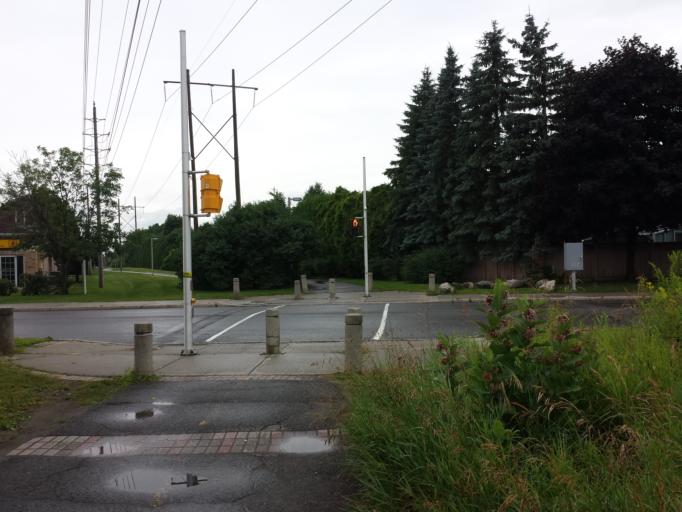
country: CA
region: Ontario
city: Bells Corners
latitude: 45.3398
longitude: -75.7715
